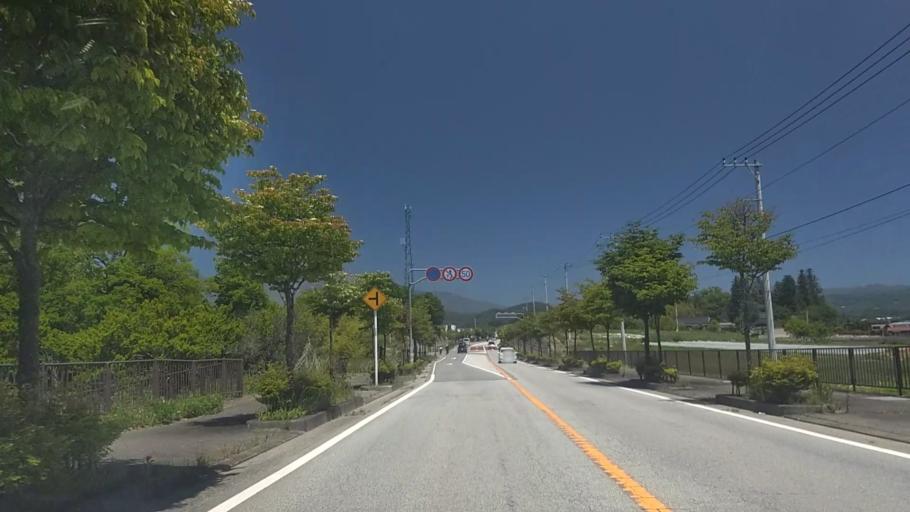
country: JP
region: Yamanashi
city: Nirasaki
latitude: 35.8208
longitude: 138.4290
